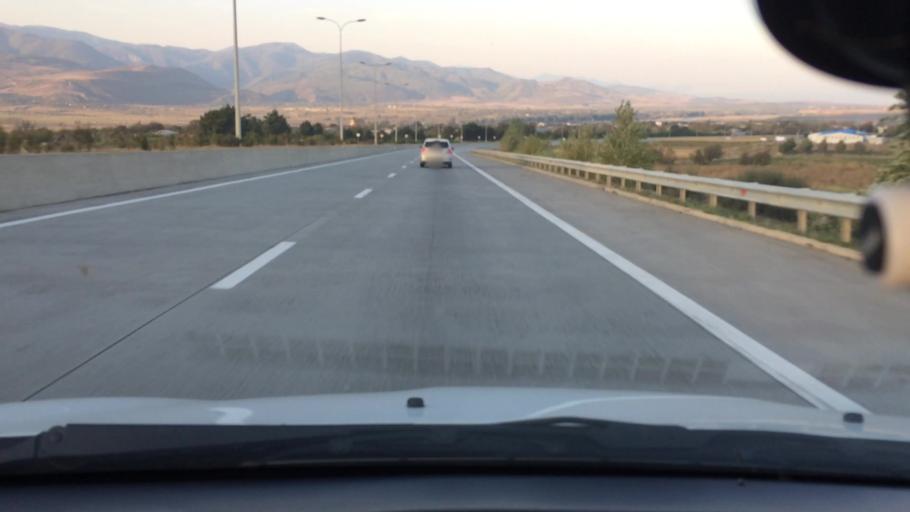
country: GE
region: Shida Kartli
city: Gori
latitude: 42.0188
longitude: 43.9965
